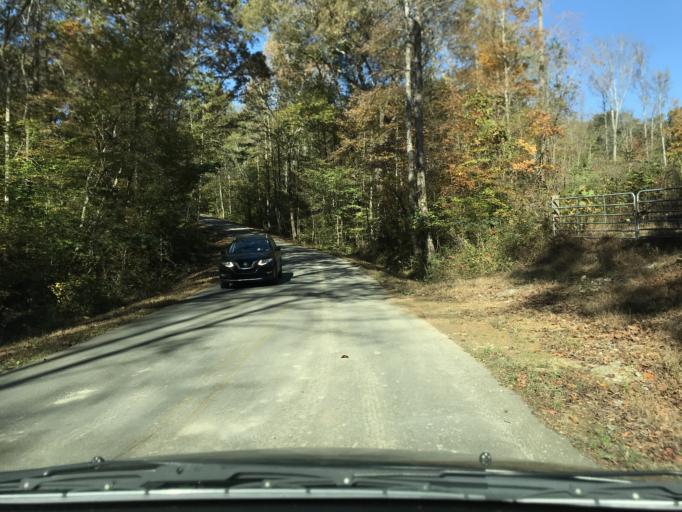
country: US
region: Georgia
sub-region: Dade County
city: Trenton
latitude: 34.9077
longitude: -85.4662
